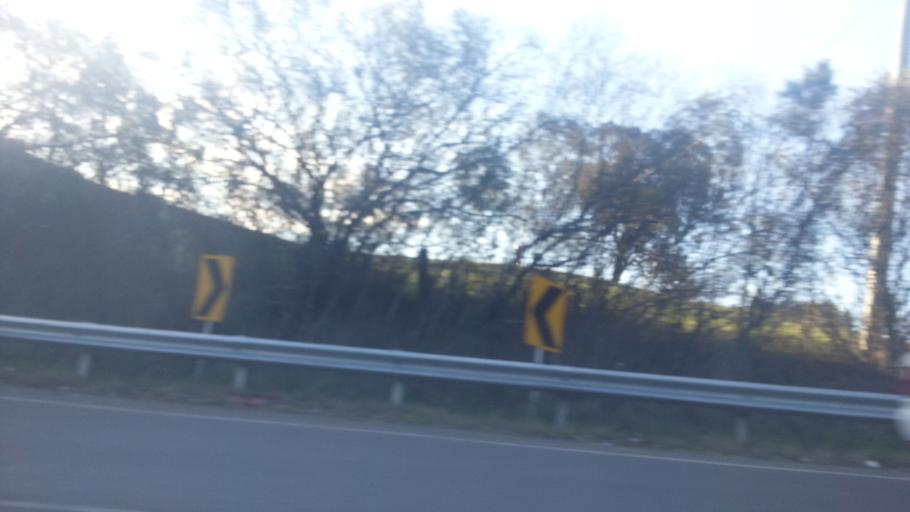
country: AU
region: New South Wales
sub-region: Wollondilly
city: Douglas Park
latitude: -34.1649
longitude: 150.7149
